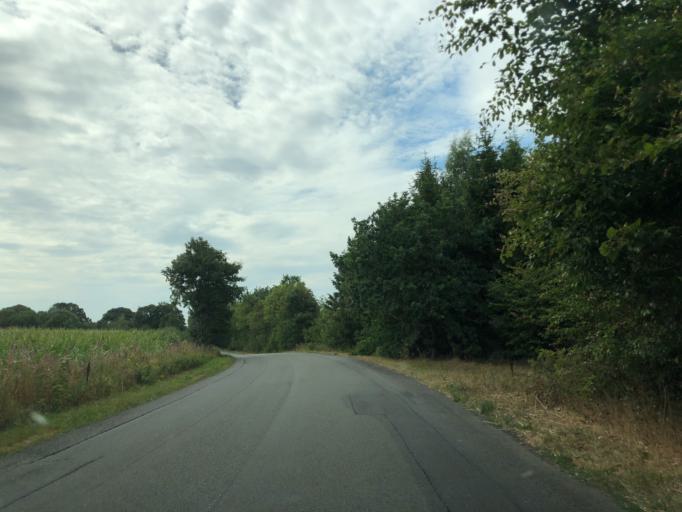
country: DK
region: South Denmark
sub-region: Vejle Kommune
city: Egtved
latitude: 55.6386
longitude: 9.1987
